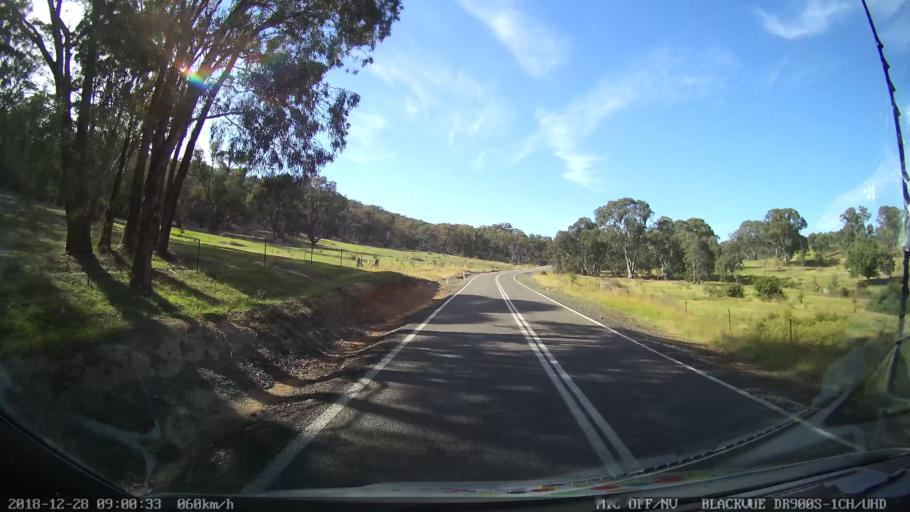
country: AU
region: New South Wales
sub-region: Upper Lachlan Shire
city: Crookwell
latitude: -34.1393
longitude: 149.3348
